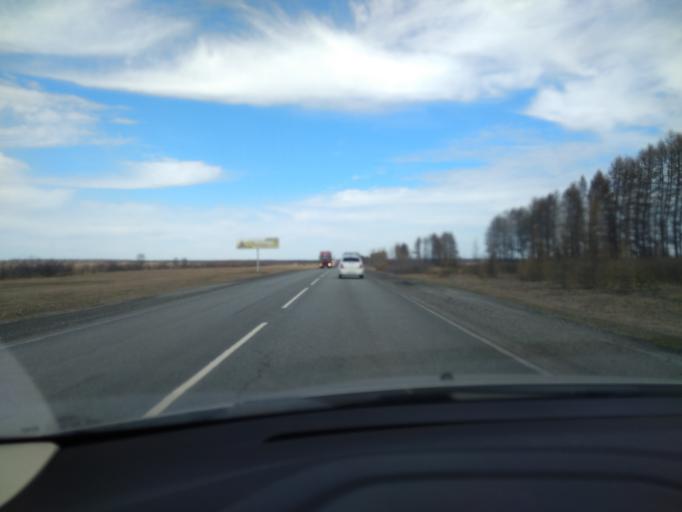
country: RU
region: Sverdlovsk
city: Pyshma
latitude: 57.0292
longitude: 63.4100
